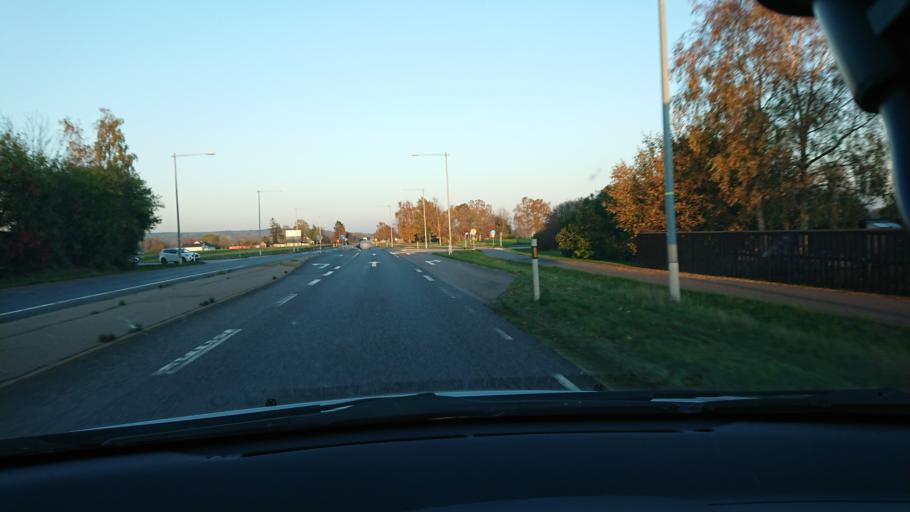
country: SE
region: Halland
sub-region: Halmstads Kommun
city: Fyllinge
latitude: 56.6850
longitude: 12.9465
